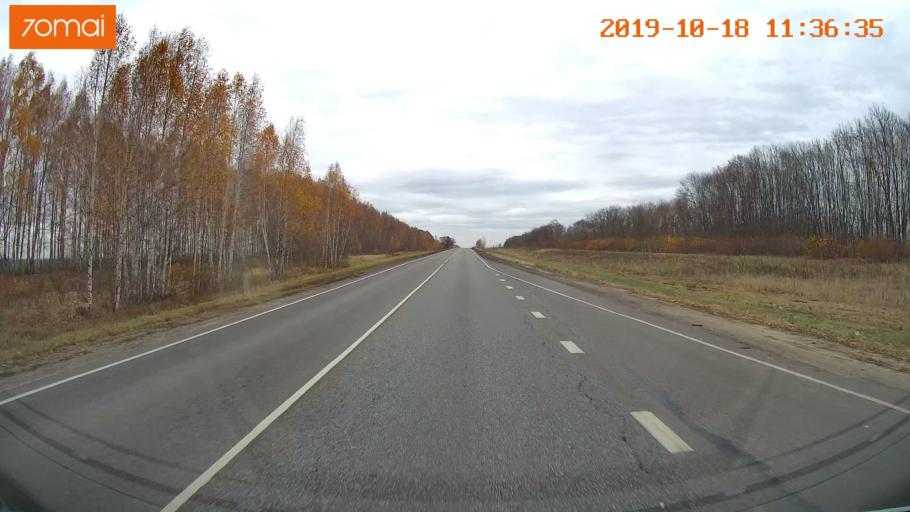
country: RU
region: Rjazan
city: Oktyabr'skiy
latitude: 54.1424
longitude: 38.8101
